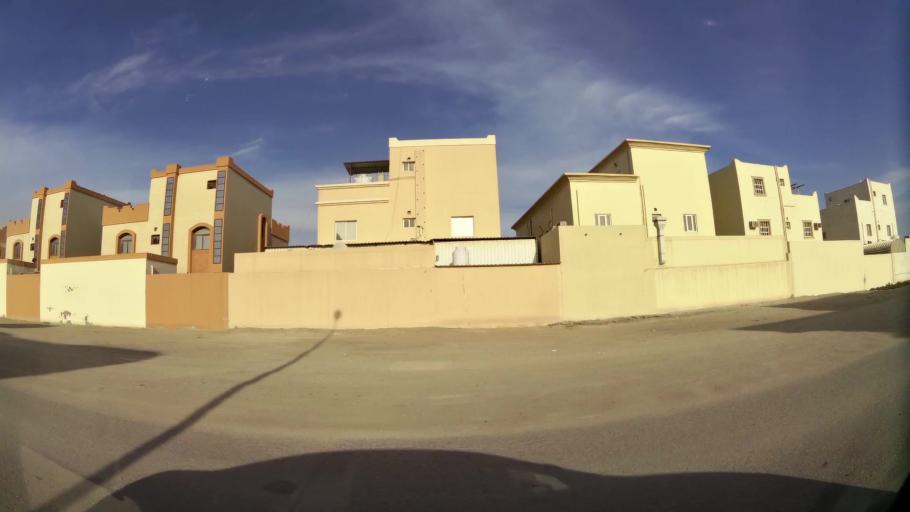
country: QA
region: Al Wakrah
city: Al Wakrah
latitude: 25.1465
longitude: 51.6060
